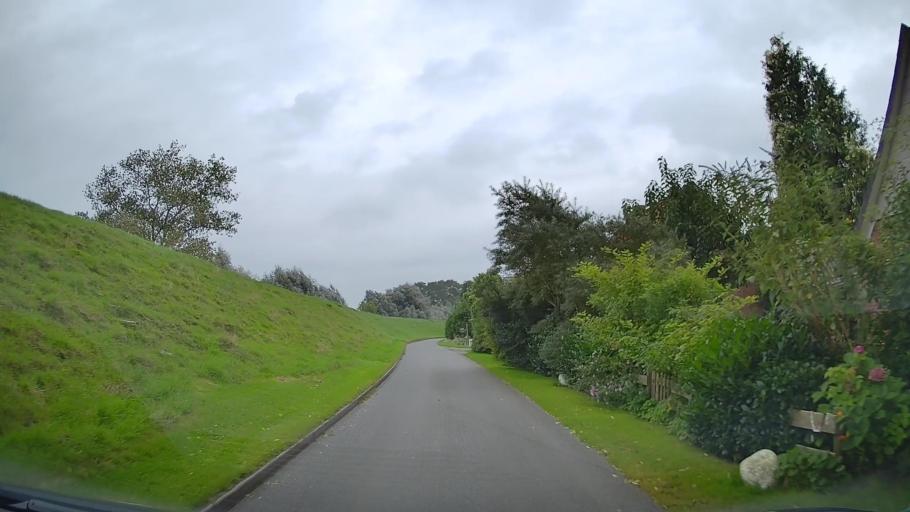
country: DE
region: Lower Saxony
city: Krummendeich
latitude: 53.8328
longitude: 9.1946
